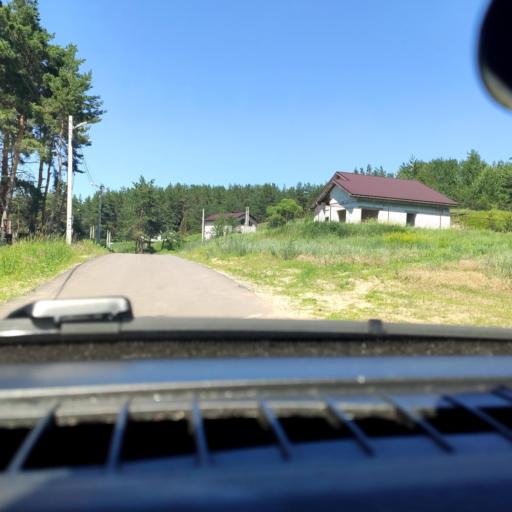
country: RU
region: Voronezj
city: Podgornoye
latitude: 51.7949
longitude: 39.1357
